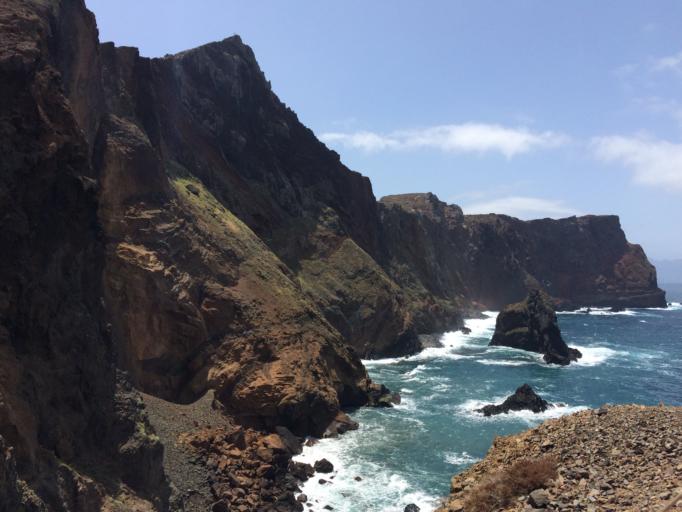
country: PT
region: Madeira
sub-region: Machico
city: Canical
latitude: 32.7490
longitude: -16.6976
